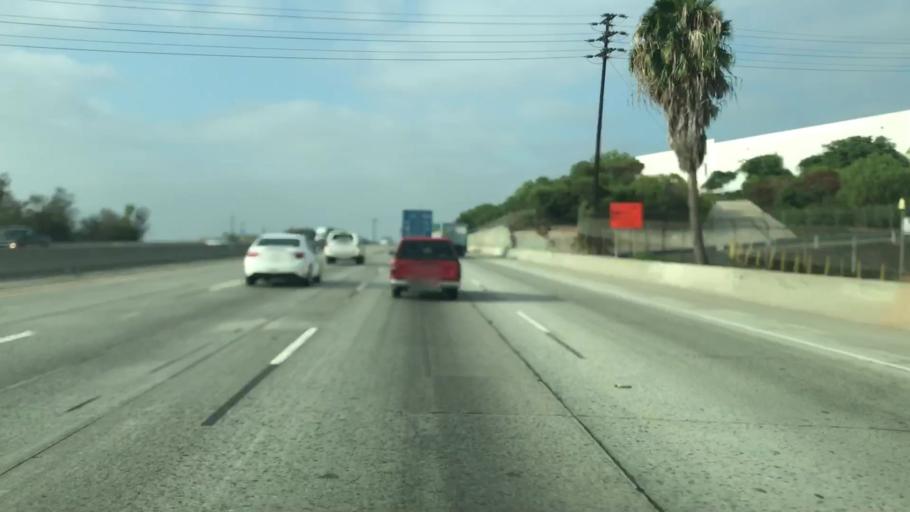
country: US
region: California
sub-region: Los Angeles County
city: San Pedro
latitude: 33.7675
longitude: -118.2820
